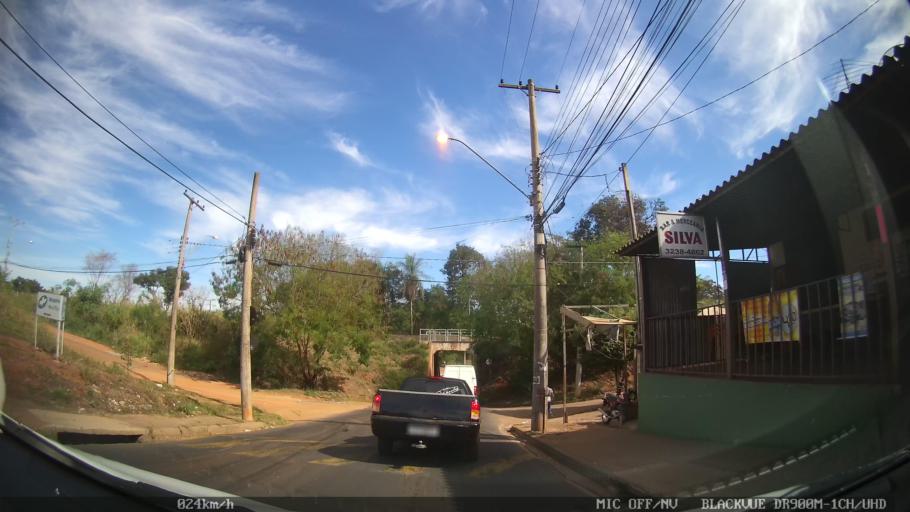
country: BR
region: Sao Paulo
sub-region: Sao Jose Do Rio Preto
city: Sao Jose do Rio Preto
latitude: -20.8422
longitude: -49.3351
